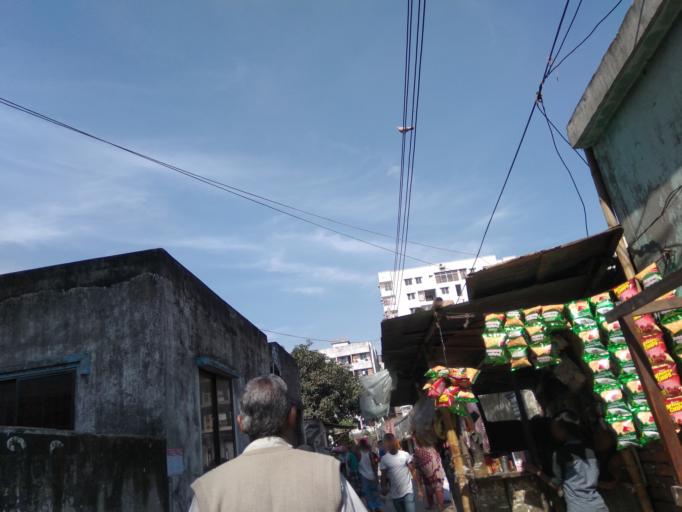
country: BD
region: Dhaka
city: Azimpur
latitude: 23.7762
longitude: 90.3600
